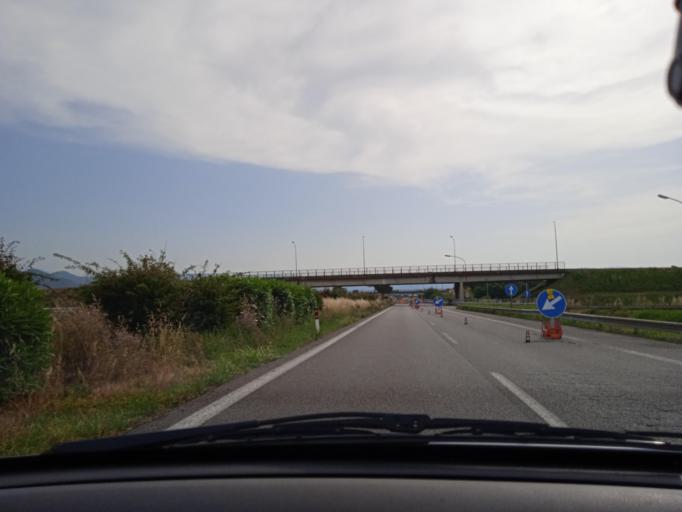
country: IT
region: Sicily
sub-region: Messina
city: Barcellona Pozzo di Gotto
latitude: 38.1570
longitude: 15.1892
